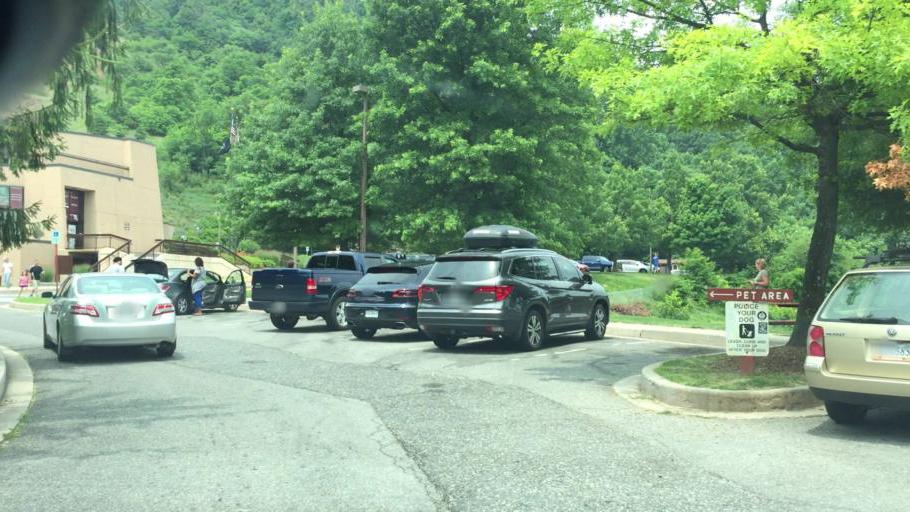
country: US
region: Maryland
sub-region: Washington County
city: Hancock
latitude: 39.7181
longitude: -78.2804
